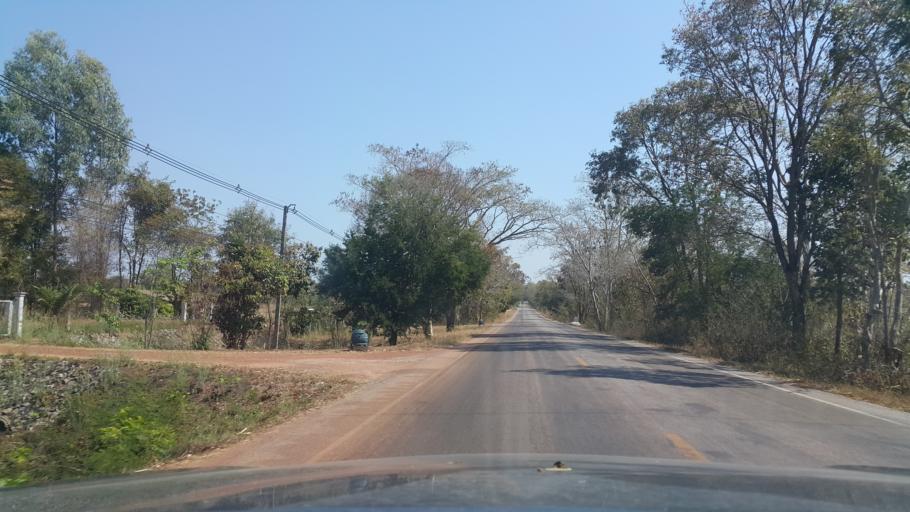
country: TH
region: Changwat Udon Thani
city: Ban Dung
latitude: 17.6093
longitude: 103.3118
